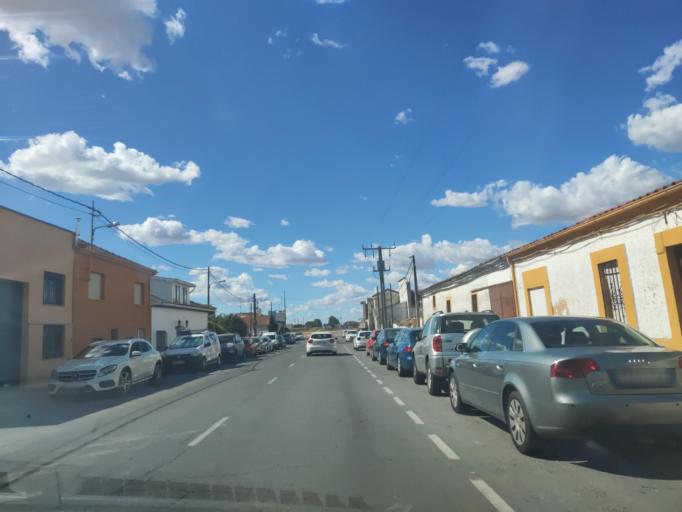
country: ES
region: Castille and Leon
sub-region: Provincia de Salamanca
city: La Fuente de San Esteban
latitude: 40.7909
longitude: -6.2433
